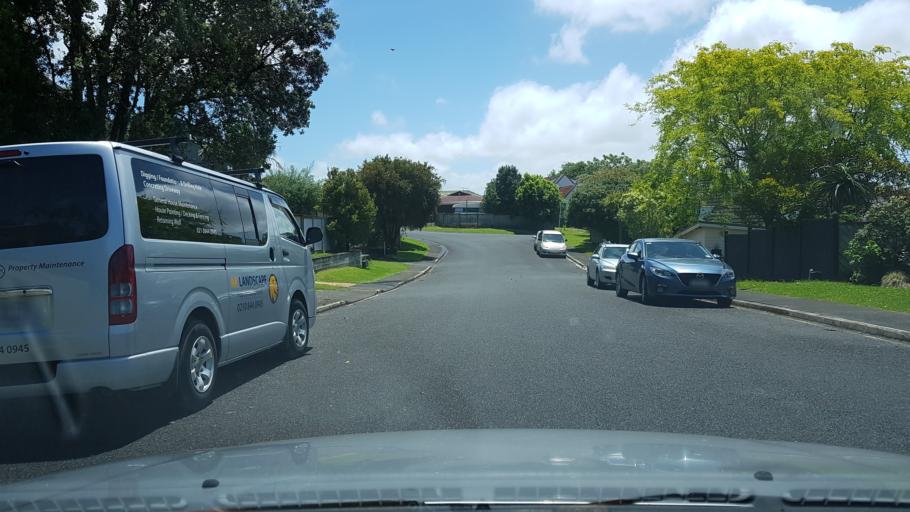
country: NZ
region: Auckland
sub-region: Auckland
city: North Shore
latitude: -36.8079
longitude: 174.7168
